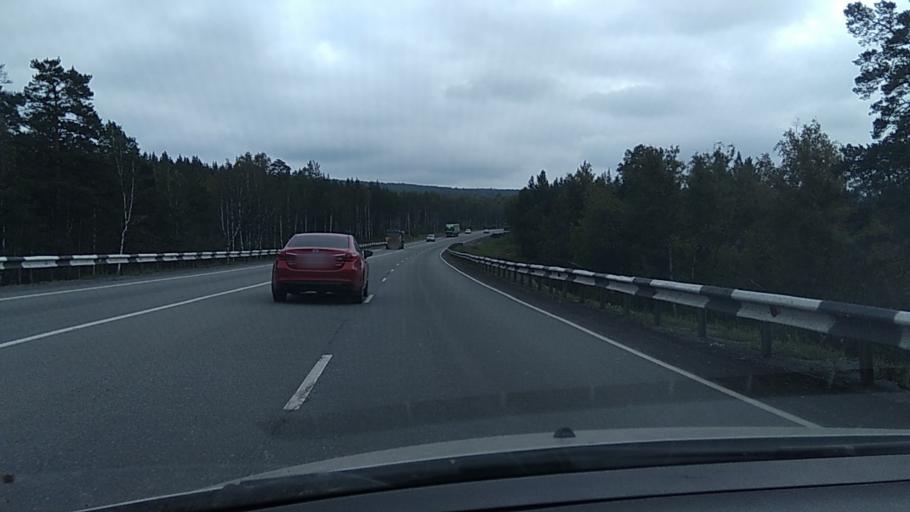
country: RU
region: Chelyabinsk
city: Zlatoust
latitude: 55.0509
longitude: 59.7199
